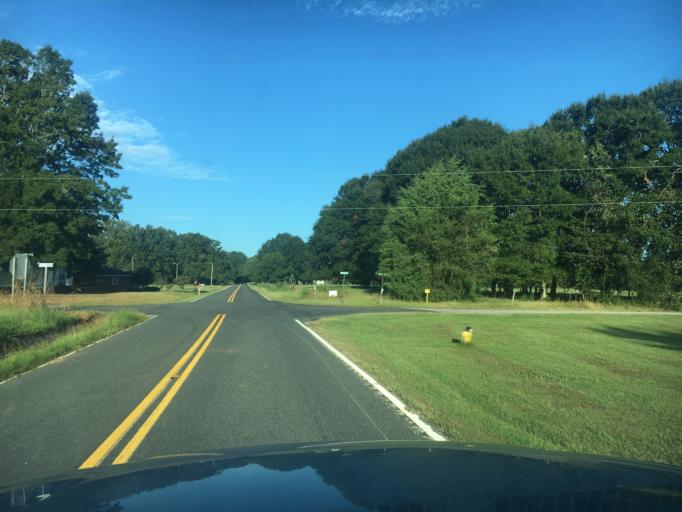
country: US
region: South Carolina
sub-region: Spartanburg County
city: Woodruff
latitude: 34.6364
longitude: -81.9933
